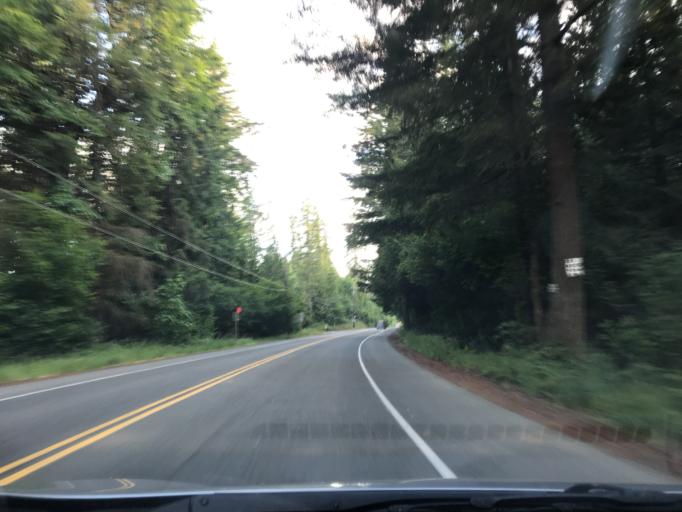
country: US
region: Washington
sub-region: King County
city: Black Diamond
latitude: 47.3024
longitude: -122.0509
